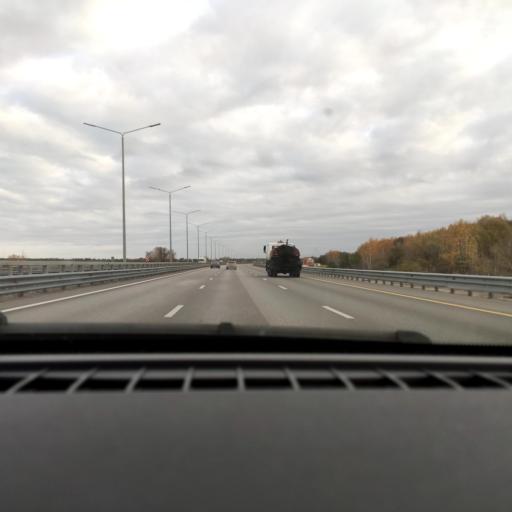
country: RU
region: Voronezj
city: Somovo
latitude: 51.7896
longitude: 39.2778
